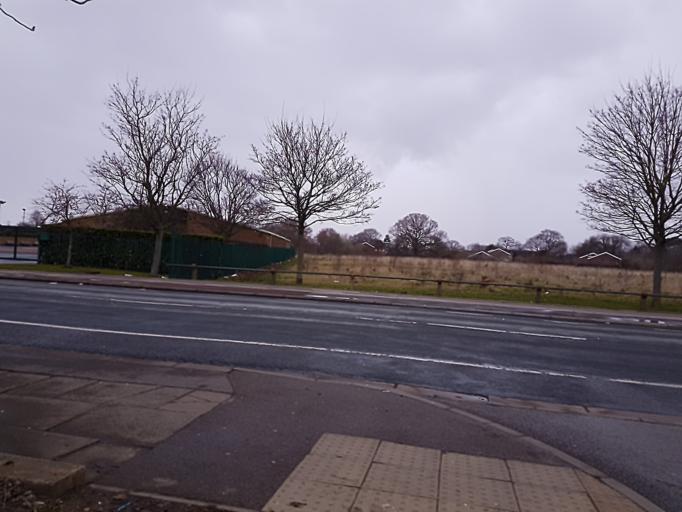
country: GB
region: England
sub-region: North East Lincolnshire
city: Grimbsy
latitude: 53.5565
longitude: -0.1013
